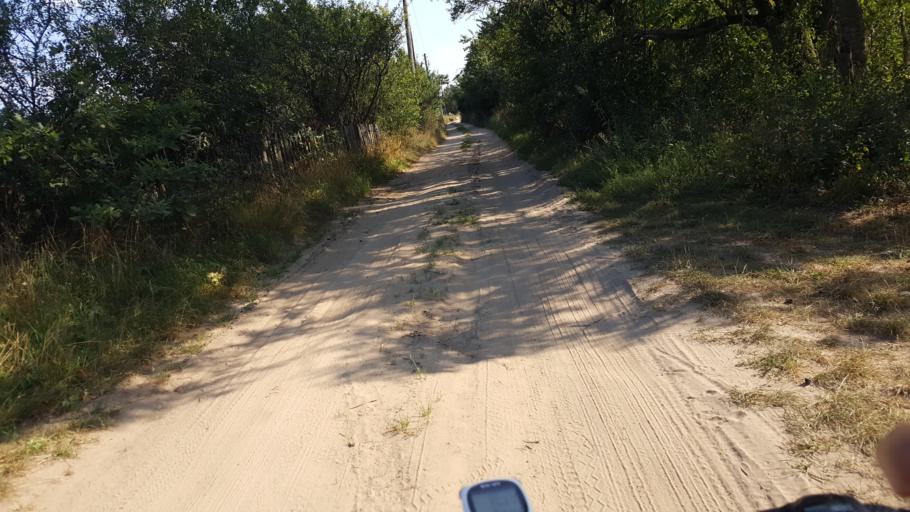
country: PL
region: Podlasie
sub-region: Powiat hajnowski
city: Hajnowka
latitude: 52.5727
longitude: 23.6274
